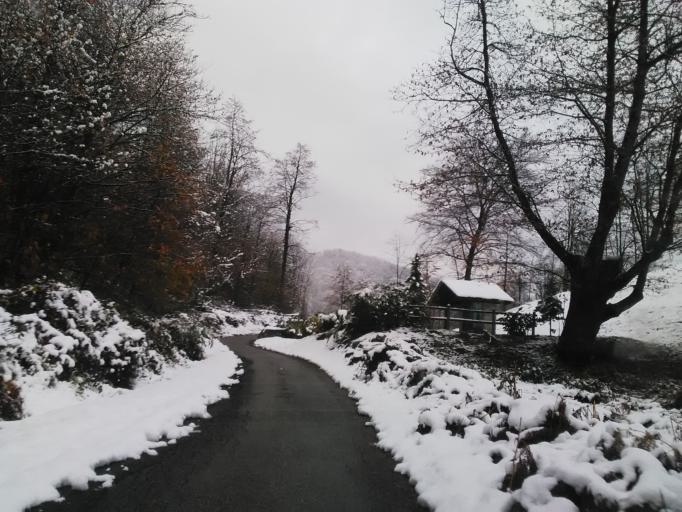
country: IT
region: Piedmont
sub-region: Provincia di Vercelli
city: Varallo
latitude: 45.7895
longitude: 8.2530
